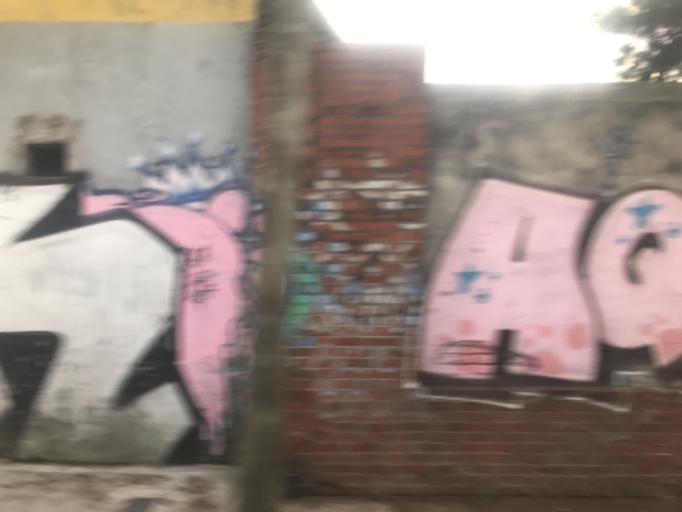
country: AR
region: Buenos Aires
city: San Justo
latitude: -34.6392
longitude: -58.5334
